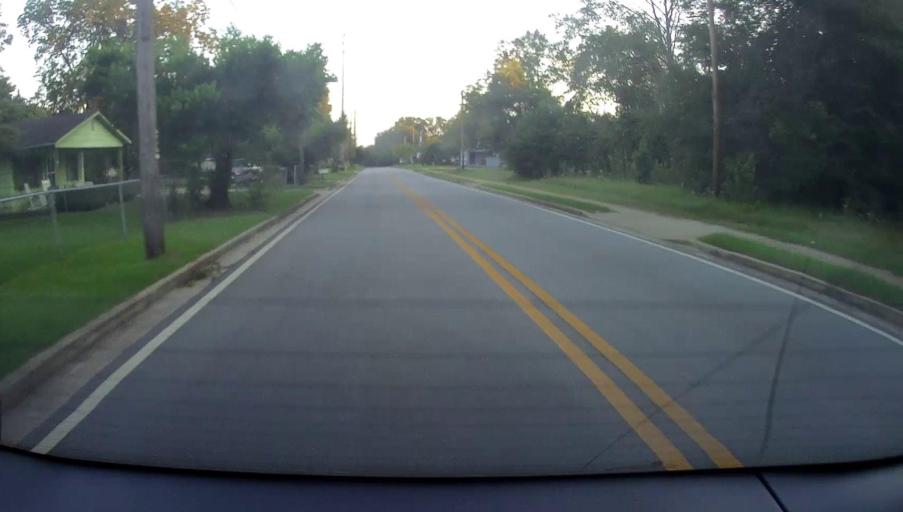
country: US
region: Georgia
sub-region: Houston County
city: Perry
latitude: 32.4635
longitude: -83.7386
